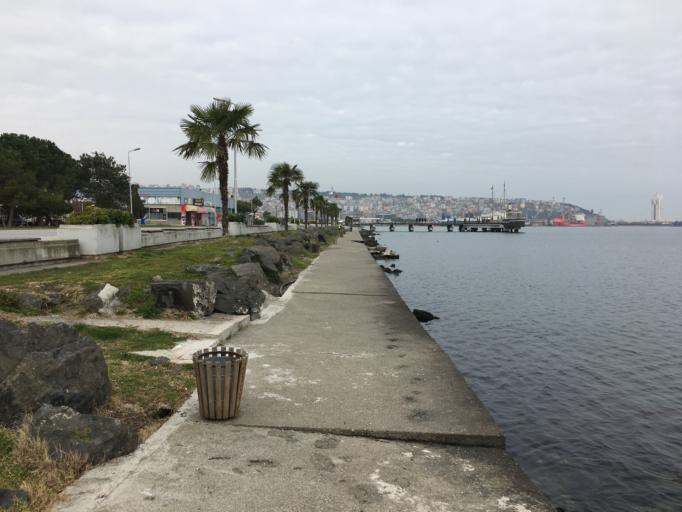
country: TR
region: Samsun
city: Samsun
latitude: 41.2915
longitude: 36.3413
